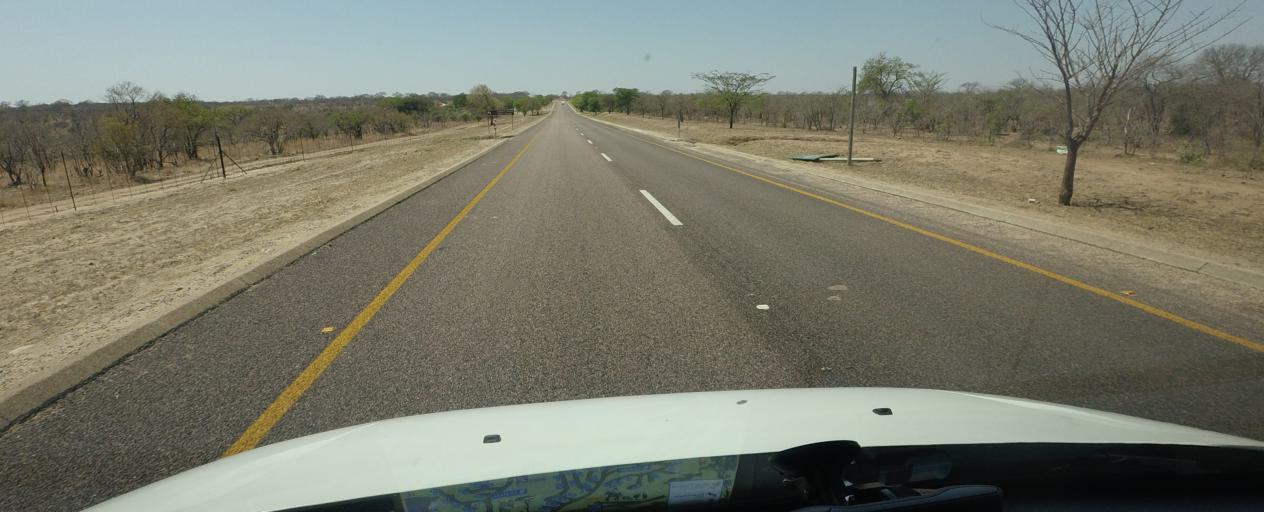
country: ZA
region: Limpopo
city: Thulamahashi
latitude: -24.5538
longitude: 31.3241
